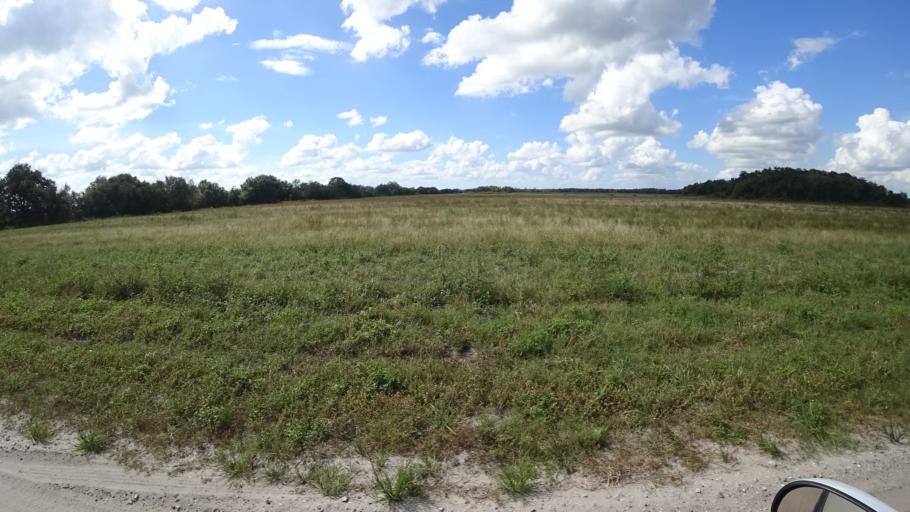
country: US
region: Florida
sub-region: DeSoto County
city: Arcadia
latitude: 27.3397
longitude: -82.1050
